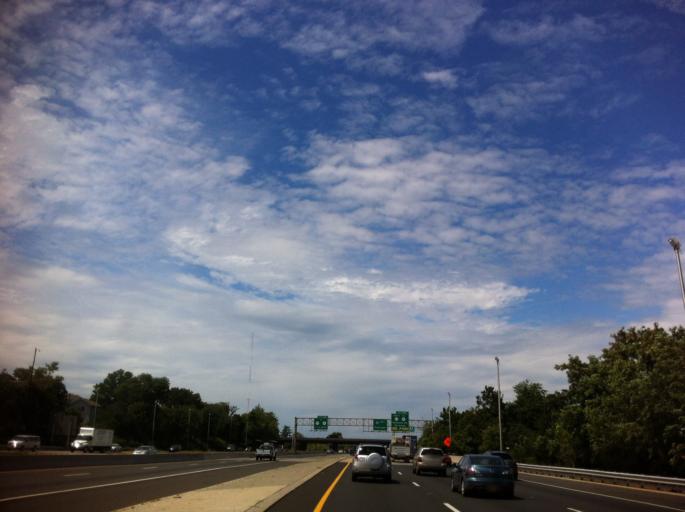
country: US
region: New Jersey
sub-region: Bergen County
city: Little Ferry
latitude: 40.8683
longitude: -74.0538
